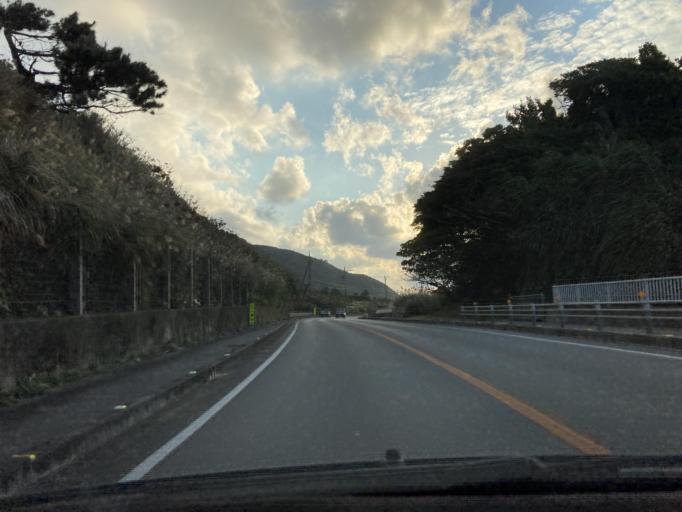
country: JP
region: Okinawa
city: Nago
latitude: 26.7832
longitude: 128.2169
